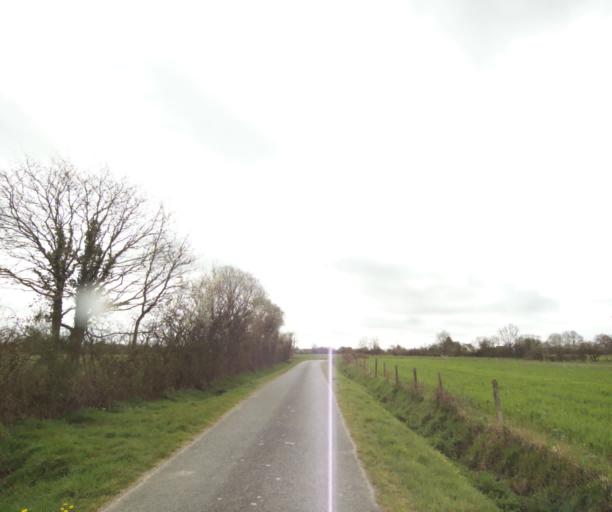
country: FR
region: Pays de la Loire
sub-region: Departement de la Loire-Atlantique
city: Bouvron
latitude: 47.4286
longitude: -1.8605
